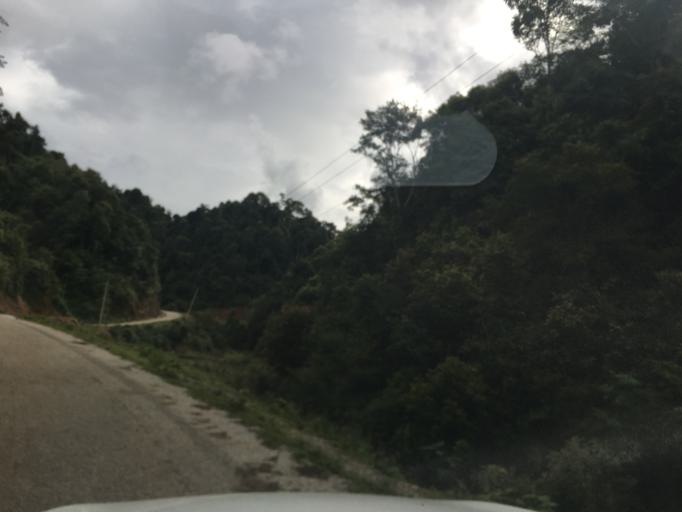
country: LA
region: Houaphan
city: Xam Nua
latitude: 20.5043
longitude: 103.9127
